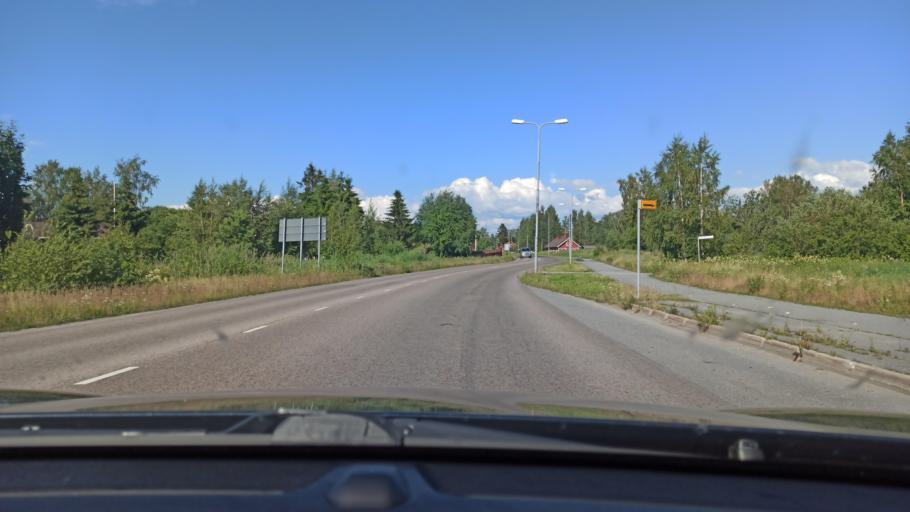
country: FI
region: Satakunta
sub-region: Pori
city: Pori
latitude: 61.5058
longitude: 21.8577
